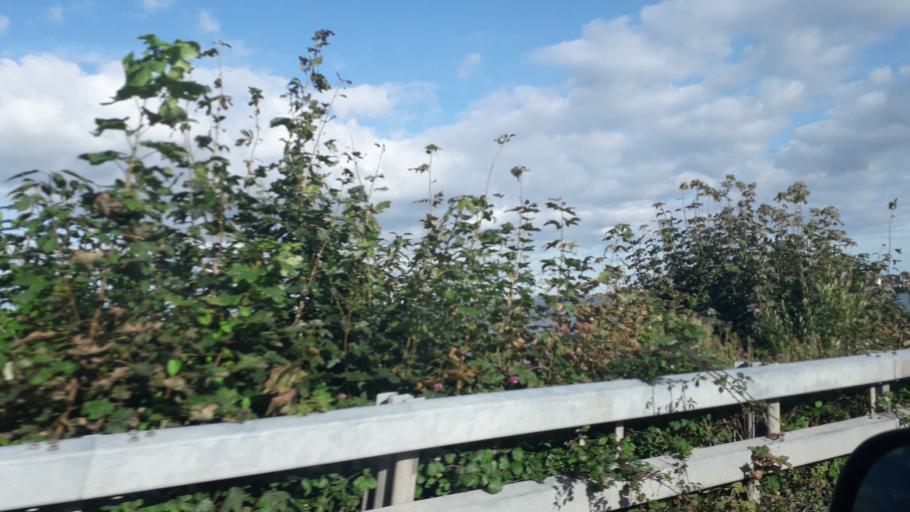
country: IE
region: Leinster
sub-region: Lu
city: Carlingford
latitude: 54.0461
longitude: -6.1894
